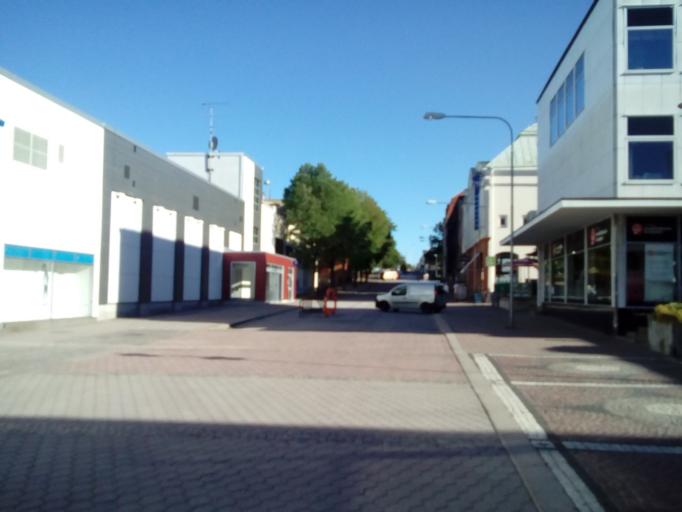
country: SE
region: Kalmar
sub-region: Vasterviks Kommun
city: Vaestervik
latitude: 57.7577
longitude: 16.6392
